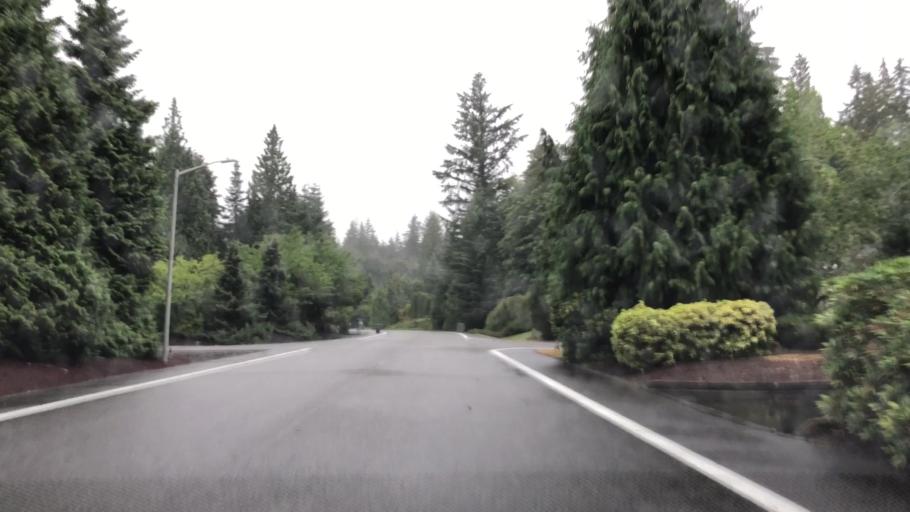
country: US
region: Washington
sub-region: Snohomish County
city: Maltby
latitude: 47.7882
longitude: -122.1253
